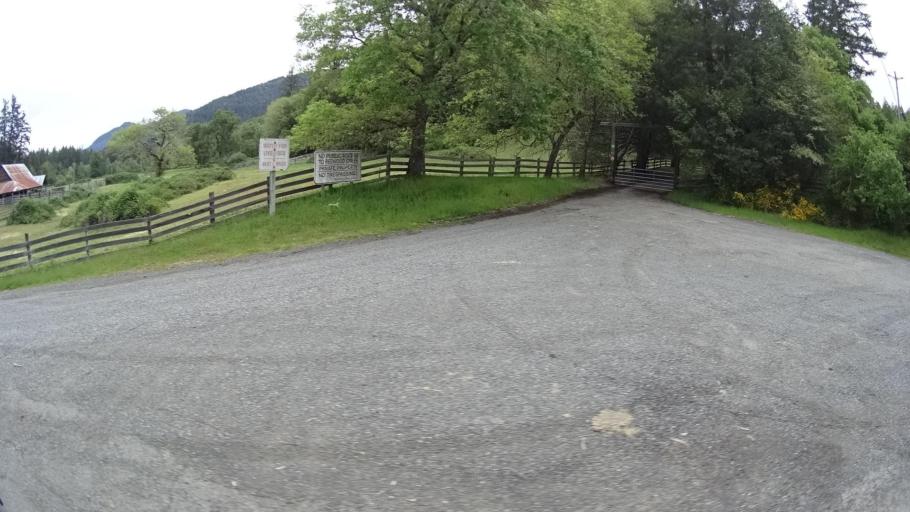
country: US
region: California
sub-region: Humboldt County
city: Blue Lake
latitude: 40.9642
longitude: -123.8413
